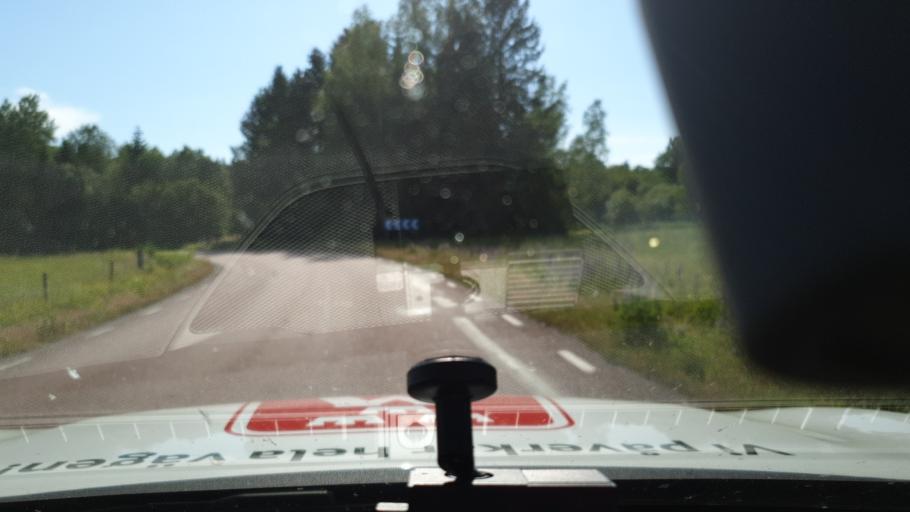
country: SE
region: Vaermland
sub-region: Kils Kommun
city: Kil
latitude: 59.4851
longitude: 13.2526
